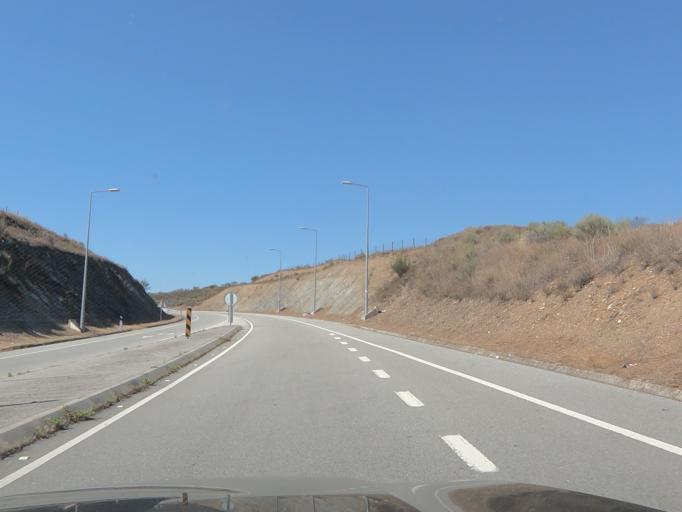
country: PT
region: Braganca
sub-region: Mirandela
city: Mirandela
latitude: 41.5174
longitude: -7.2288
